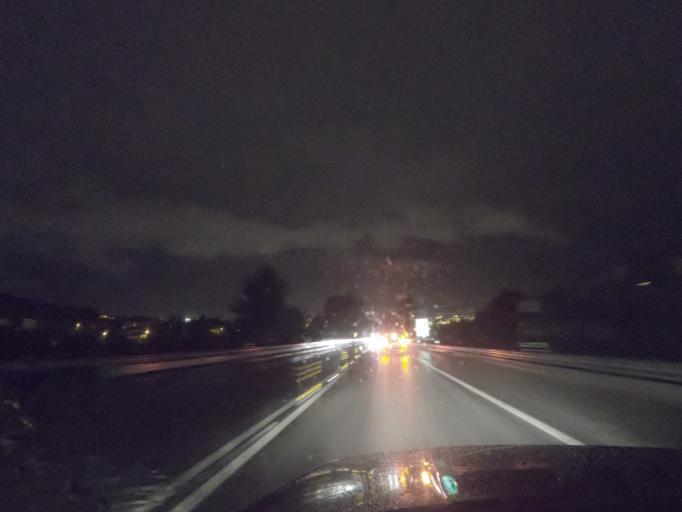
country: PT
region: Vila Real
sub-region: Vila Real
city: Vila Real
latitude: 41.3163
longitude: -7.7147
